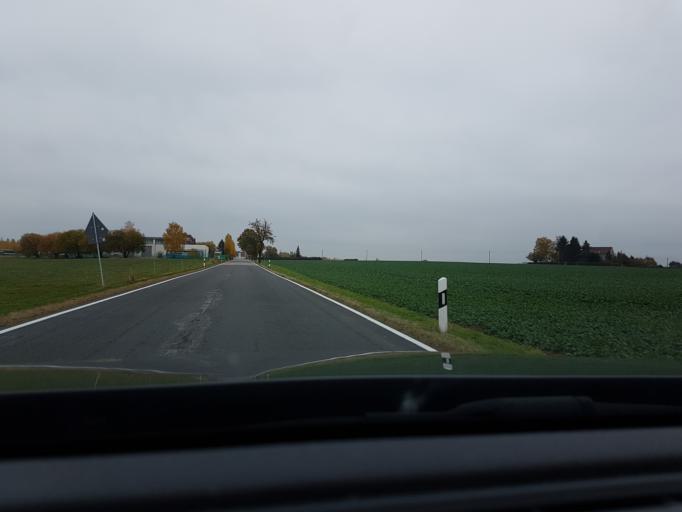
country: DE
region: Saxony
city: Altmittweida
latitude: 50.9840
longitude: 12.9413
